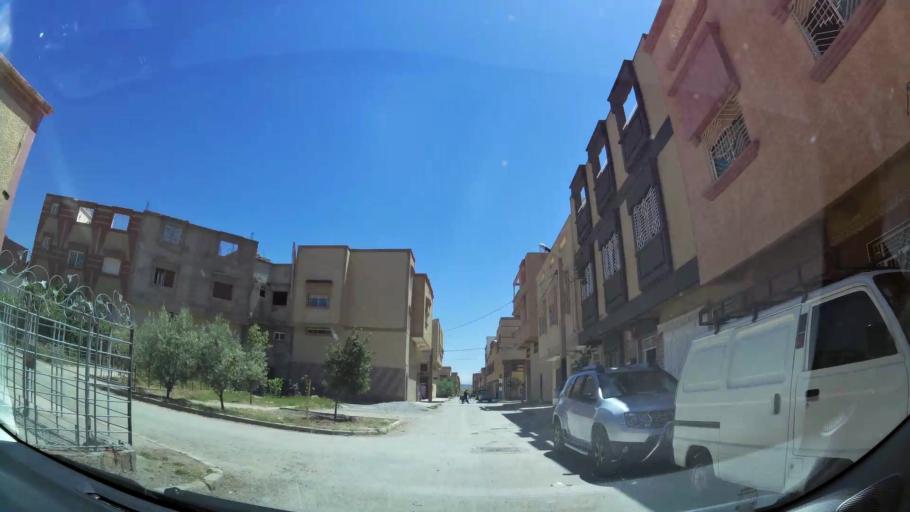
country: MA
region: Oriental
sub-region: Oujda-Angad
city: Oujda
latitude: 34.6762
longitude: -1.8591
